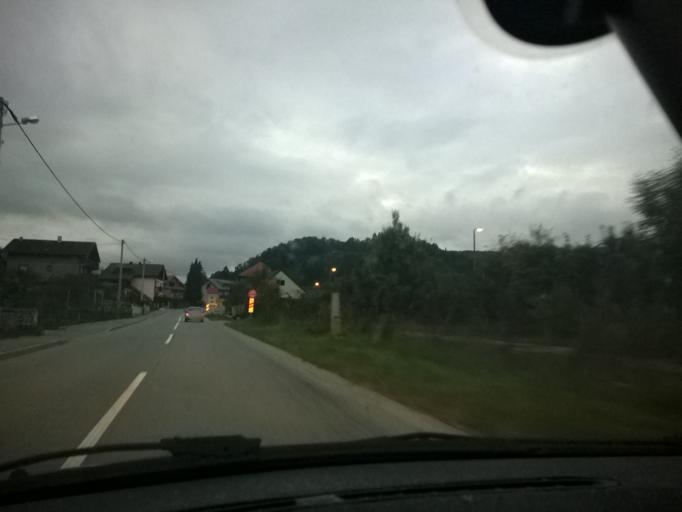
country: HR
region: Krapinsko-Zagorska
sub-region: Grad Krapina
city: Krapina
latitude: 46.1940
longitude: 15.8417
